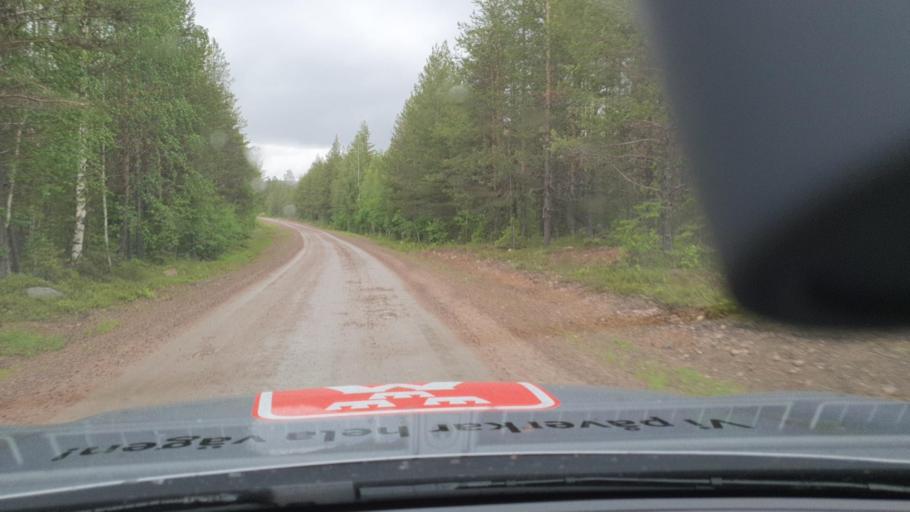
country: SE
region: Norrbotten
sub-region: Overkalix Kommun
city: OEverkalix
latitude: 66.6370
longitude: 22.7103
